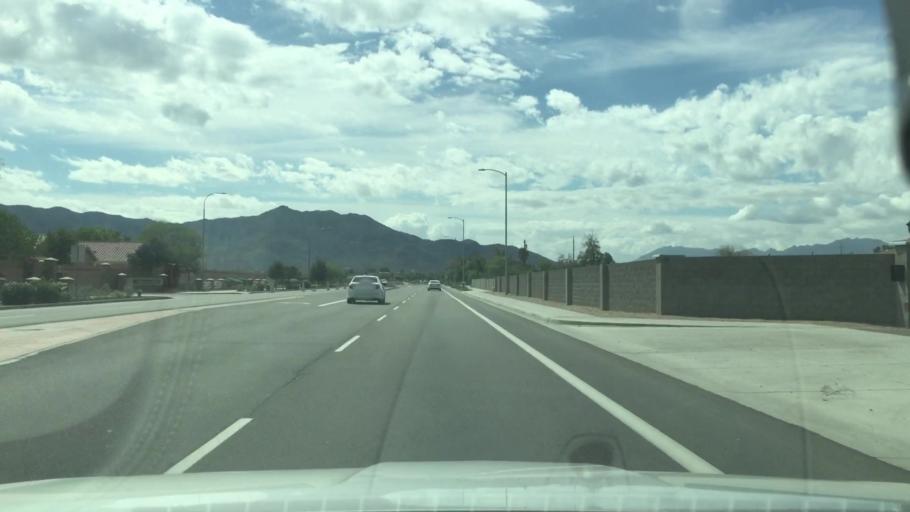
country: US
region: Arizona
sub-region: Maricopa County
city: Laveen
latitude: 33.3840
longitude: -112.1338
